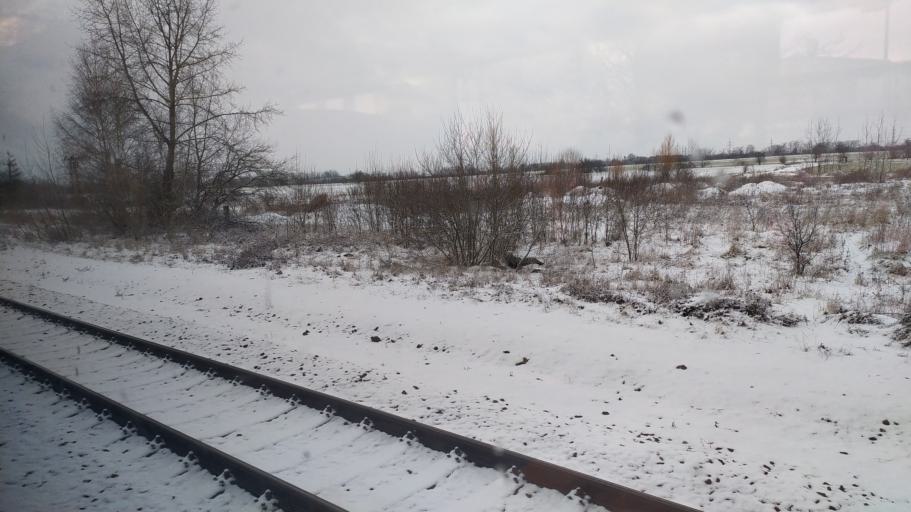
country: CZ
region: Central Bohemia
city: Rudna
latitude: 50.0396
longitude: 14.2428
